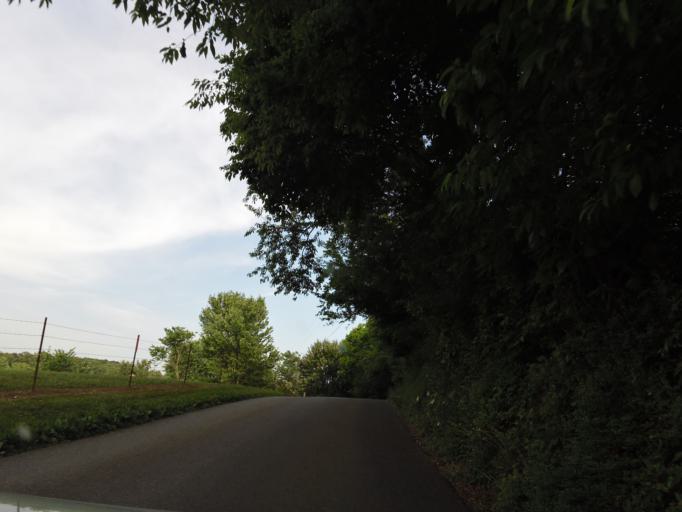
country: US
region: Tennessee
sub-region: Sevier County
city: Seymour
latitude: 35.8523
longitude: -83.7998
